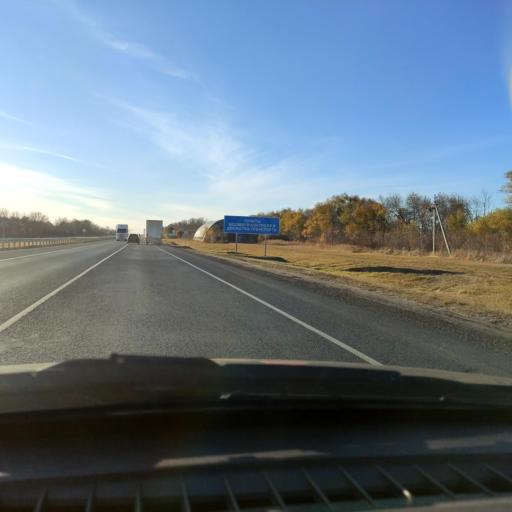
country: RU
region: Samara
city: Varlamovo
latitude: 53.1952
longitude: 48.2695
